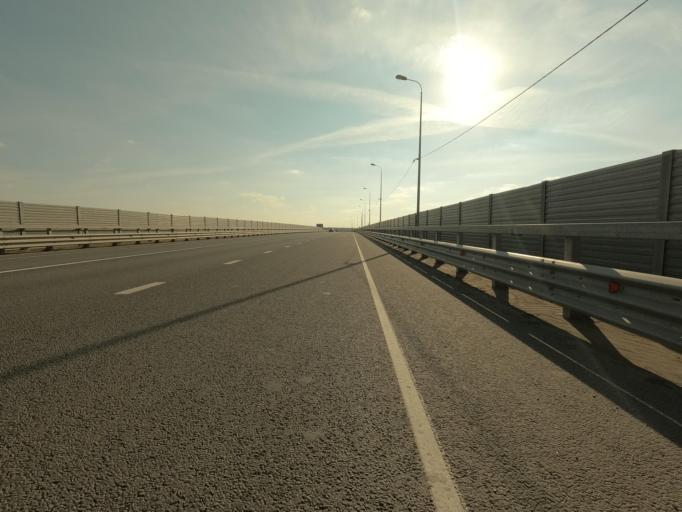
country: RU
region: Leningrad
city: Mga
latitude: 59.7556
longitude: 31.0923
